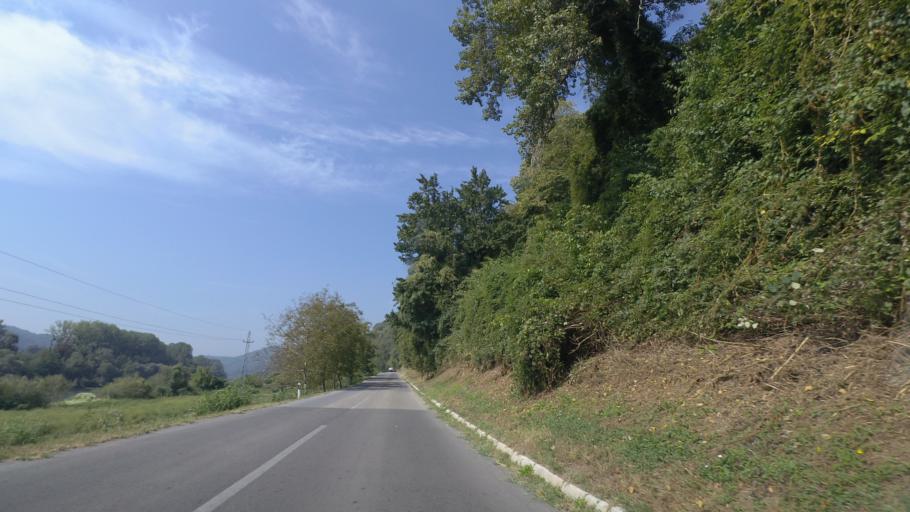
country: BA
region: Republika Srpska
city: Kostajnica
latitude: 45.2230
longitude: 16.5146
